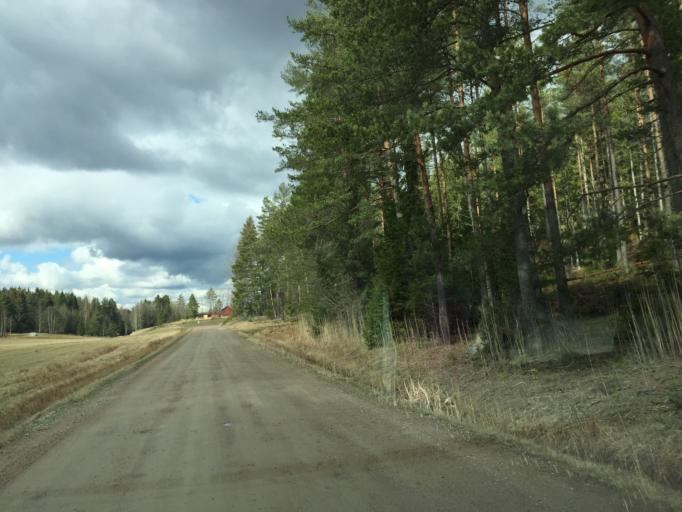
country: SE
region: Soedermanland
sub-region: Nykopings Kommun
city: Nykoping
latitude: 58.9585
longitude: 17.0517
